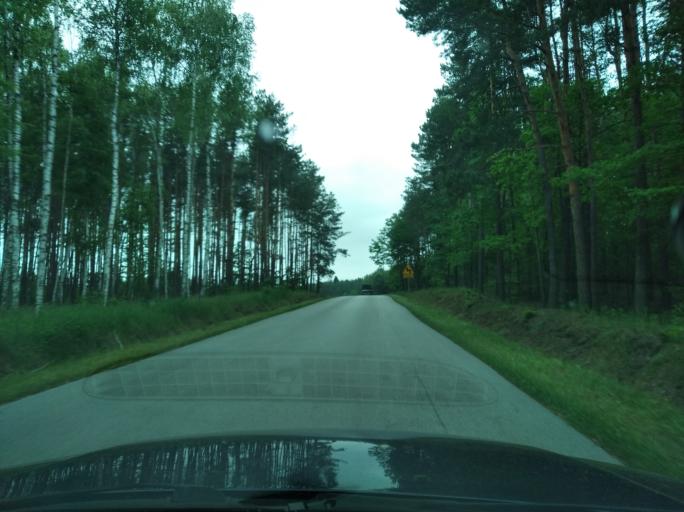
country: PL
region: Subcarpathian Voivodeship
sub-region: Powiat kolbuszowski
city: Niwiska
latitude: 50.2121
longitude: 21.6361
